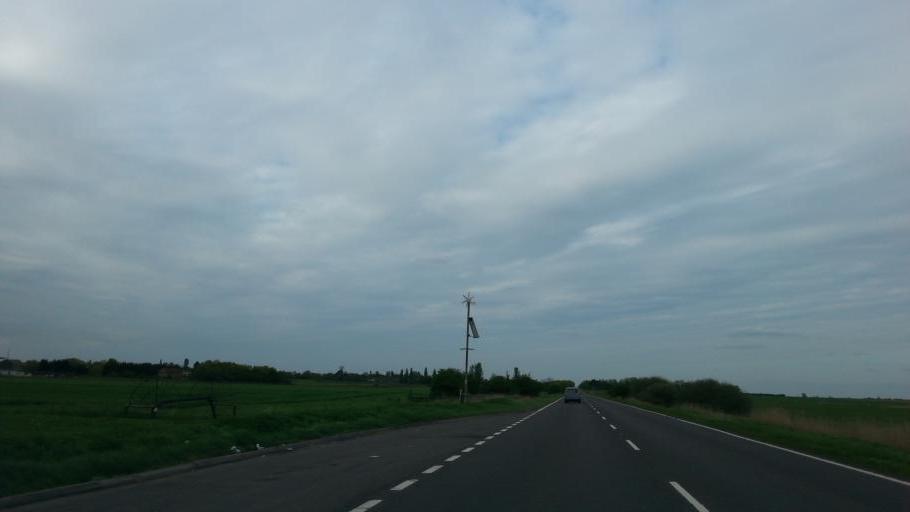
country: GB
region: England
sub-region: Cambridgeshire
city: Doddington
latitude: 52.4819
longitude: 0.0600
